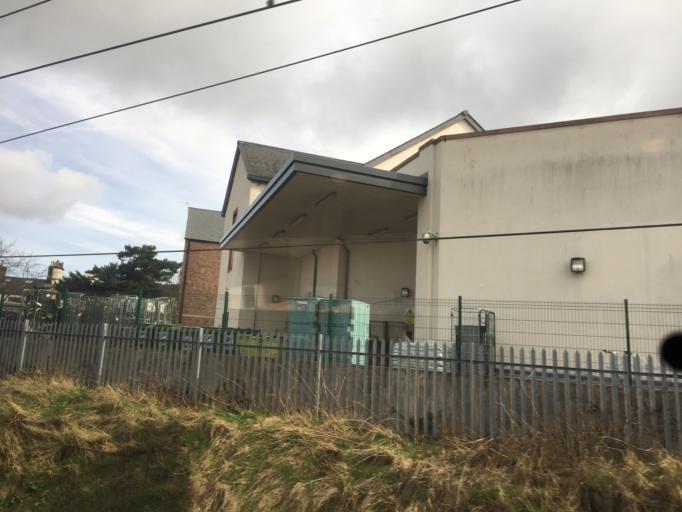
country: GB
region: England
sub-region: Cumbria
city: Penrith
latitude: 54.6648
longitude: -2.7587
